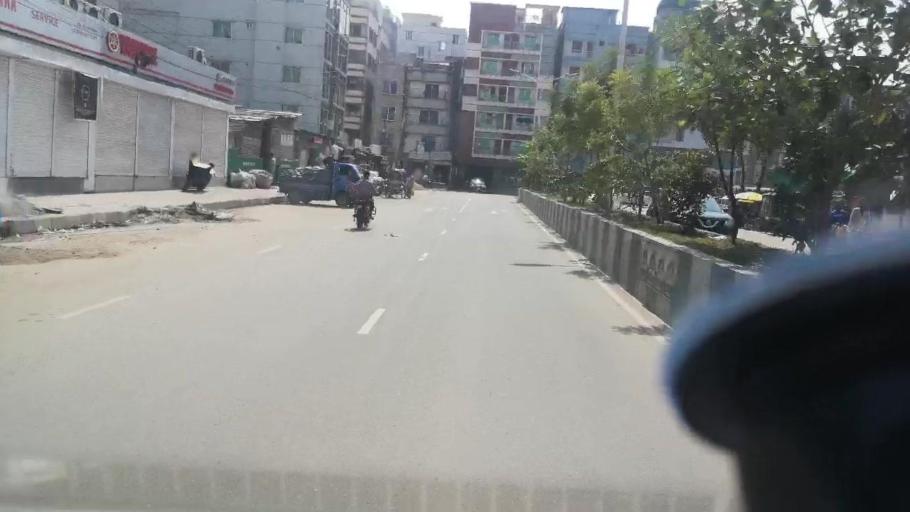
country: BD
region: Dhaka
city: Tungi
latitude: 23.8712
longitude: 90.3797
